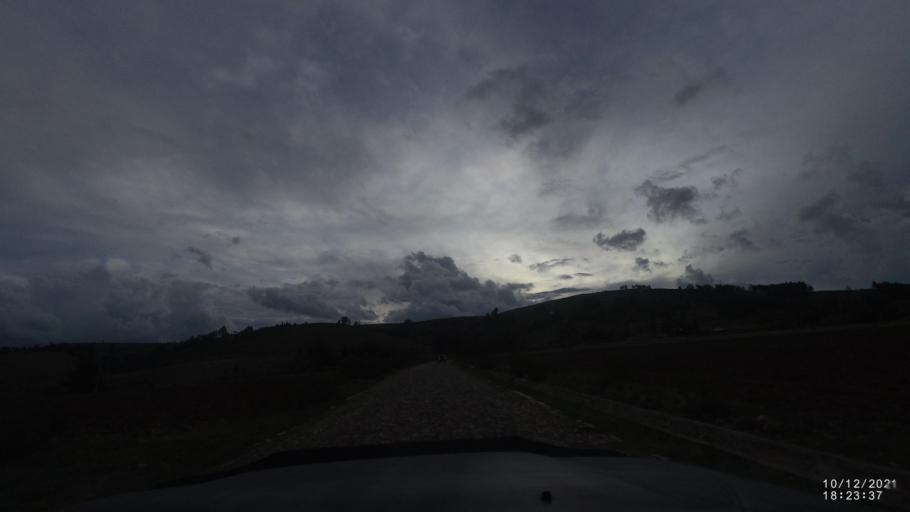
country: BO
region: Cochabamba
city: Tarata
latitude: -17.7865
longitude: -65.9690
